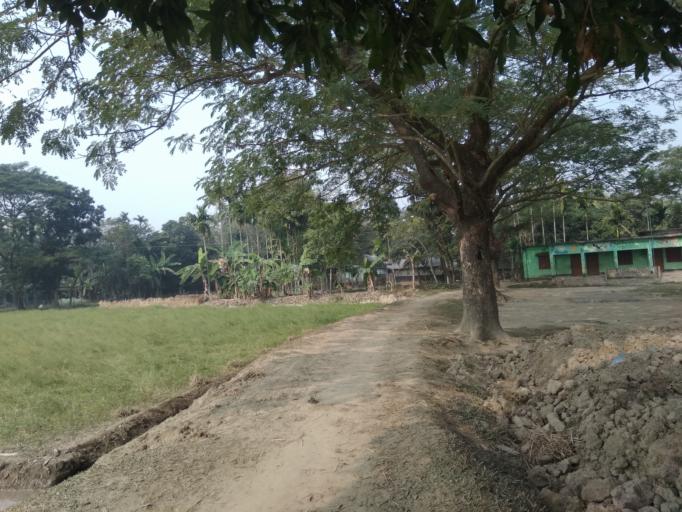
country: BD
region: Dhaka
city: Netrakona
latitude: 24.8932
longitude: 90.6647
